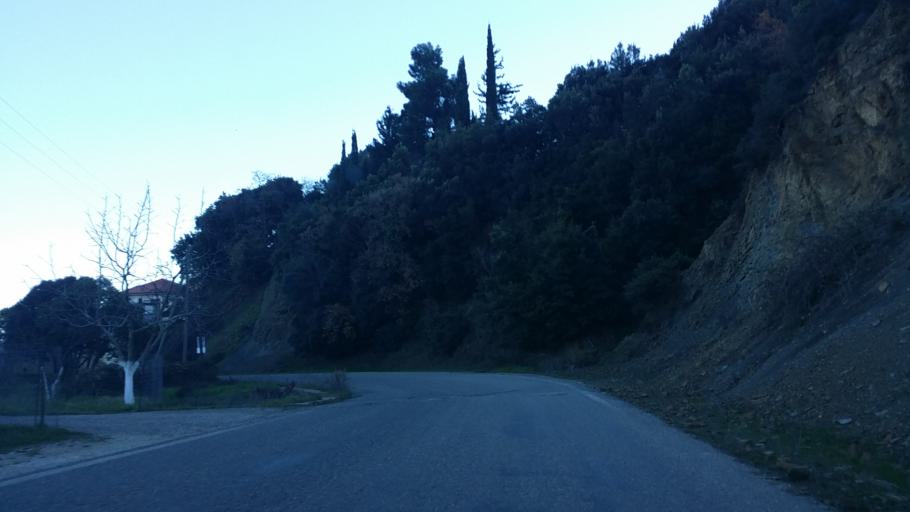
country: GR
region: West Greece
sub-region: Nomos Aitolias kai Akarnanias
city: Sardinia
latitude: 38.8699
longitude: 21.2841
